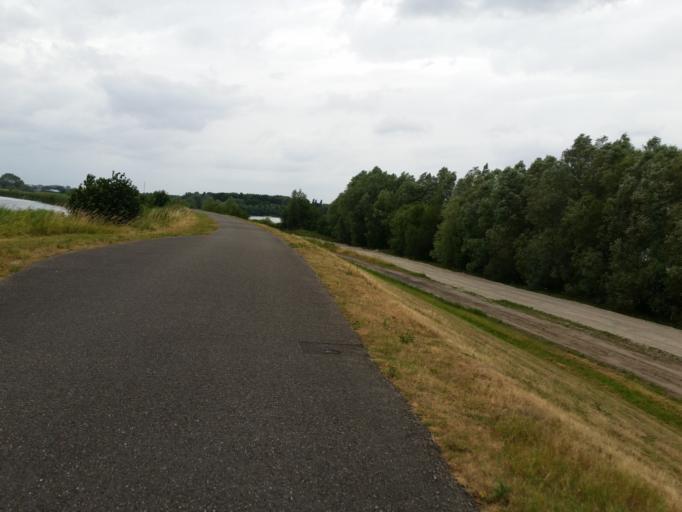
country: BE
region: Flanders
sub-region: Provincie Antwerpen
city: Rumst
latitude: 51.0582
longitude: 4.4427
